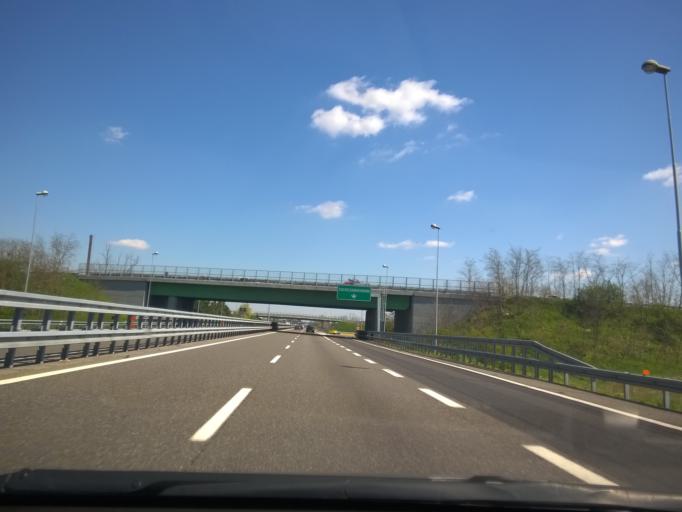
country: IT
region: Emilia-Romagna
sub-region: Provincia di Piacenza
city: Castel San Giovanni
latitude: 45.0759
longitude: 9.4482
